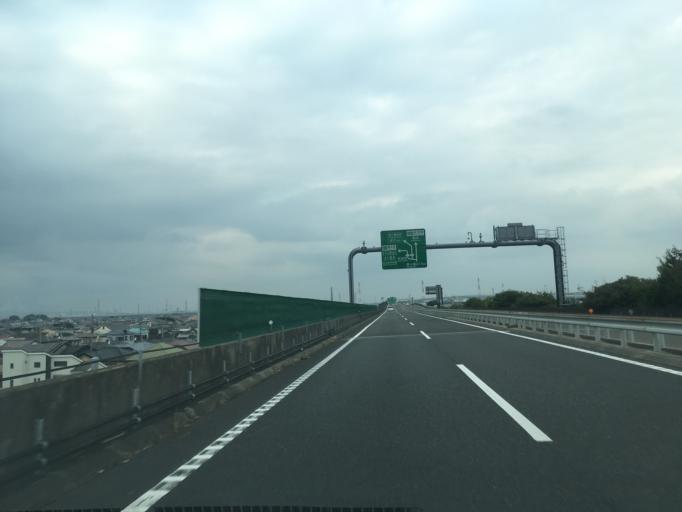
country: JP
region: Kanagawa
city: Chigasaki
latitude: 35.3380
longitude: 139.3870
